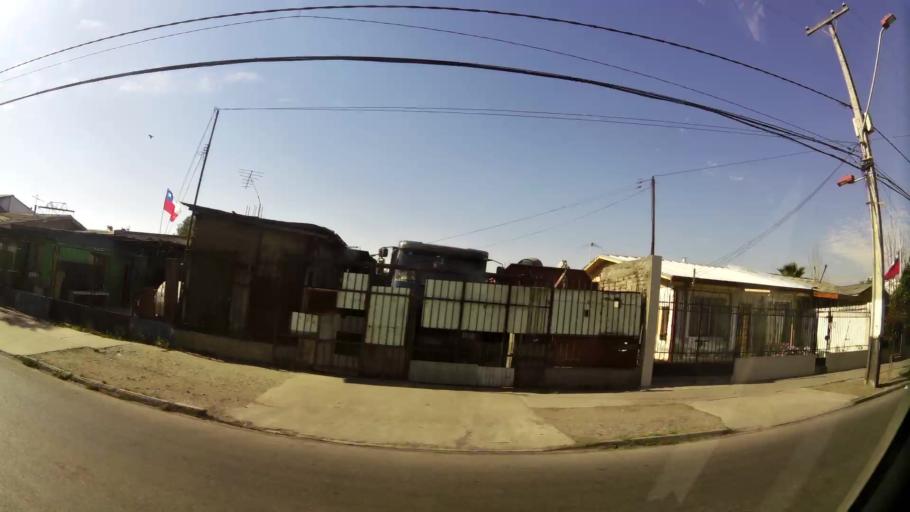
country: CL
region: Santiago Metropolitan
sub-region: Provincia de Santiago
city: Santiago
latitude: -33.5039
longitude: -70.6897
